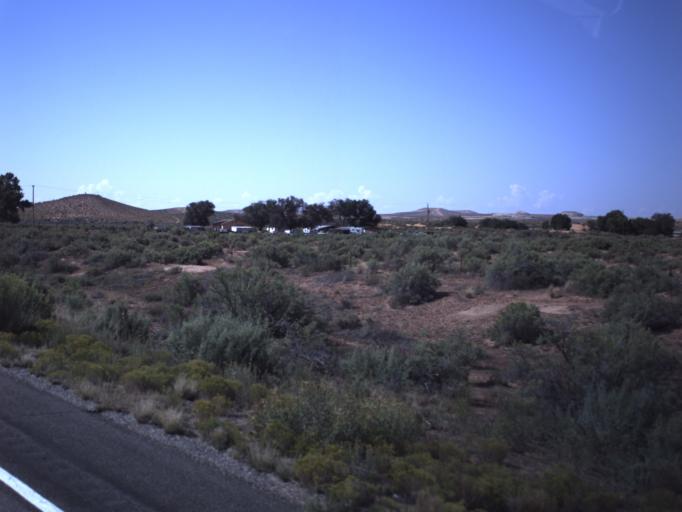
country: US
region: Utah
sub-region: San Juan County
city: Blanding
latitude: 37.1059
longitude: -109.5466
